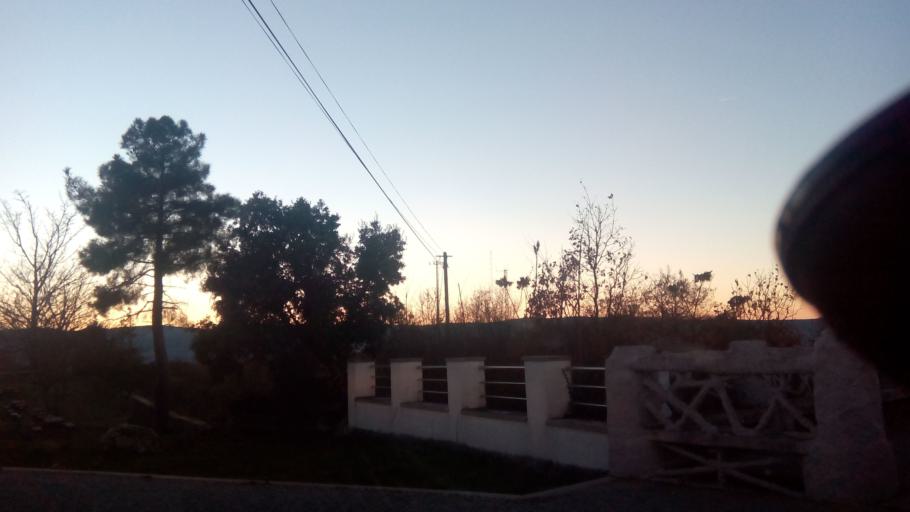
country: PT
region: Braganca
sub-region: Braganca Municipality
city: Braganca
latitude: 41.7958
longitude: -6.7471
